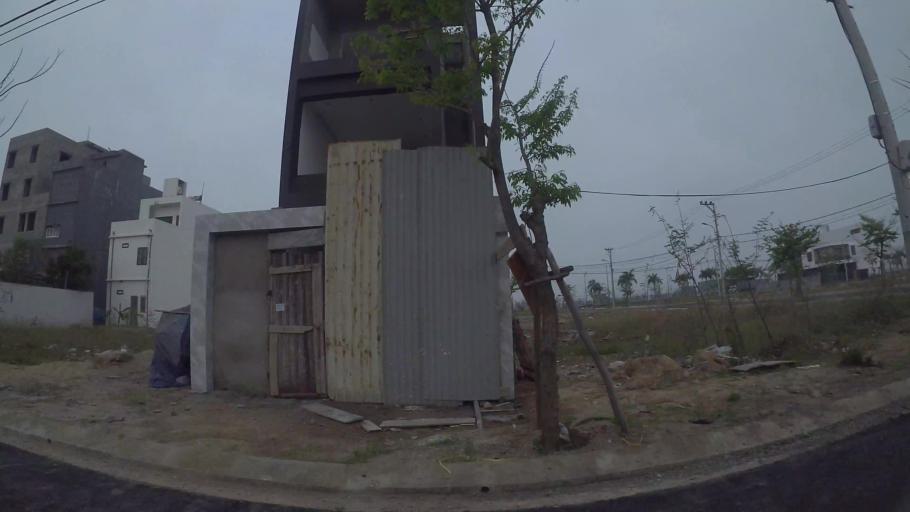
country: VN
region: Da Nang
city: Ngu Hanh Son
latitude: 16.0218
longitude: 108.2339
